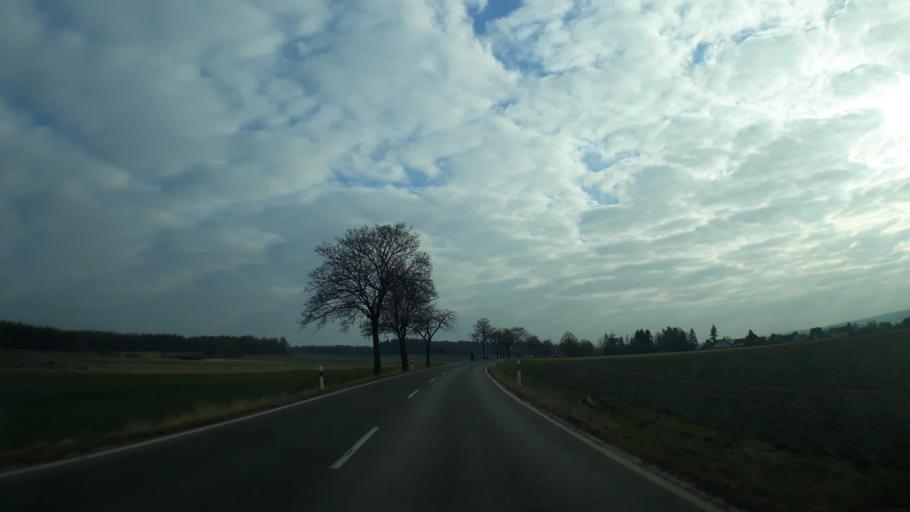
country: DE
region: North Rhine-Westphalia
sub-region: Regierungsbezirk Koln
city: Bad Munstereifel
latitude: 50.6106
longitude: 6.7390
